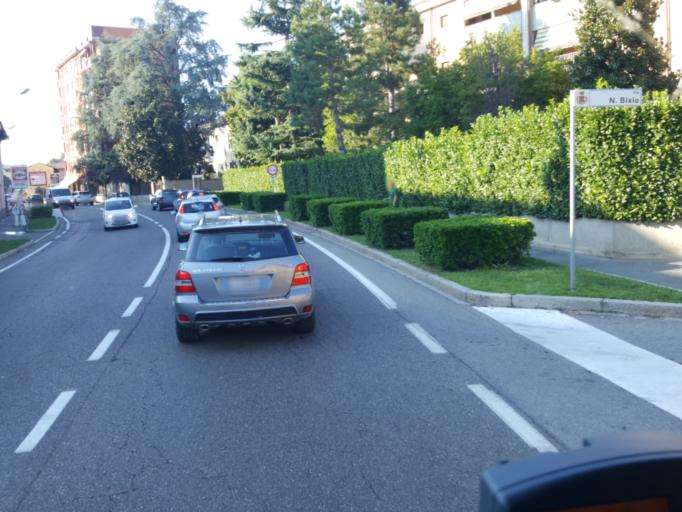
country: IT
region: Lombardy
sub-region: Citta metropolitana di Milano
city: San Vittore Olona
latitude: 45.5822
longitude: 8.9485
